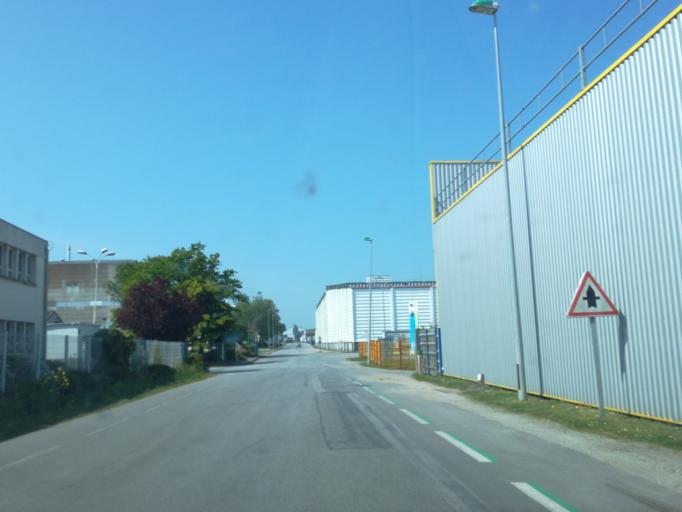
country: FR
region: Brittany
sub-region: Departement du Morbihan
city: Le Sourn
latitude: 48.0484
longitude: -2.9614
